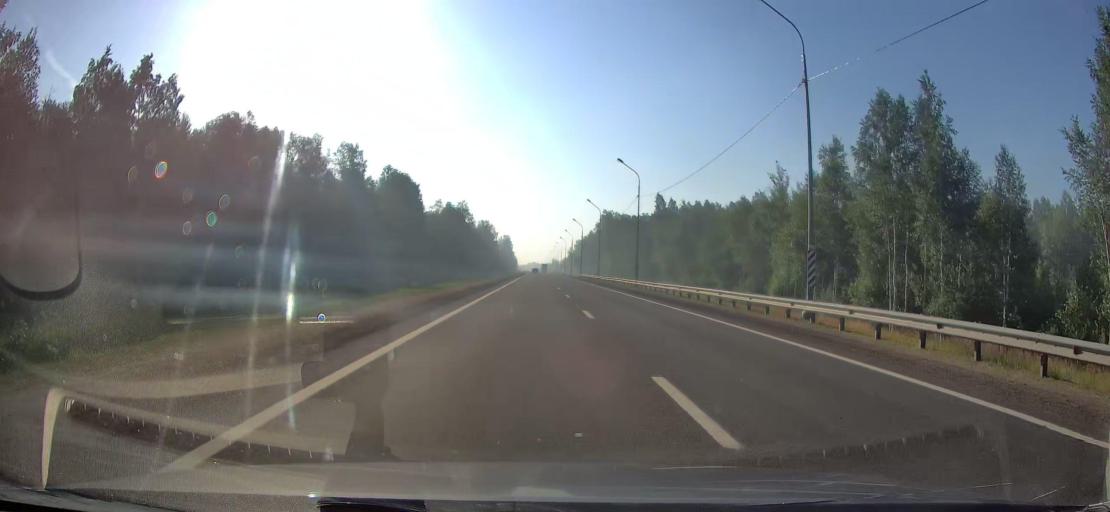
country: RU
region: Leningrad
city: Sinyavino
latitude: 59.8925
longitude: 31.1444
